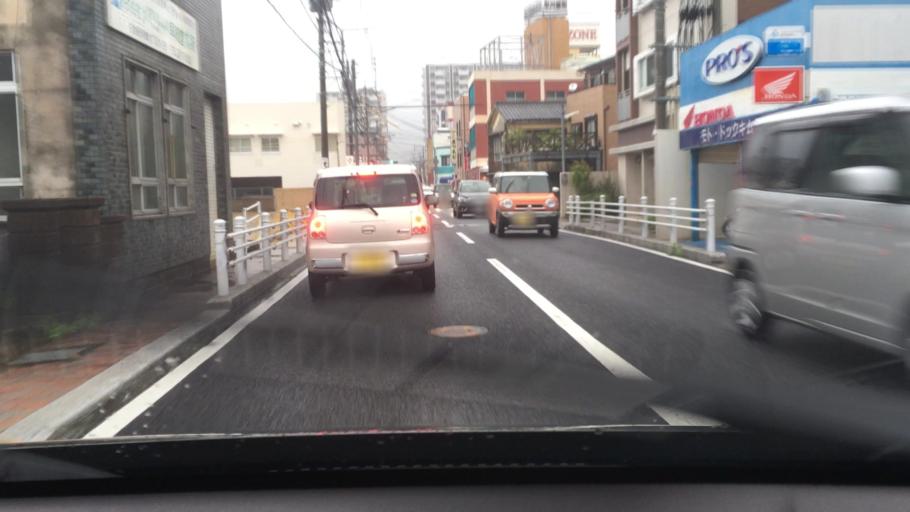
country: JP
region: Nagasaki
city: Sasebo
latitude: 33.1323
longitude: 129.7984
